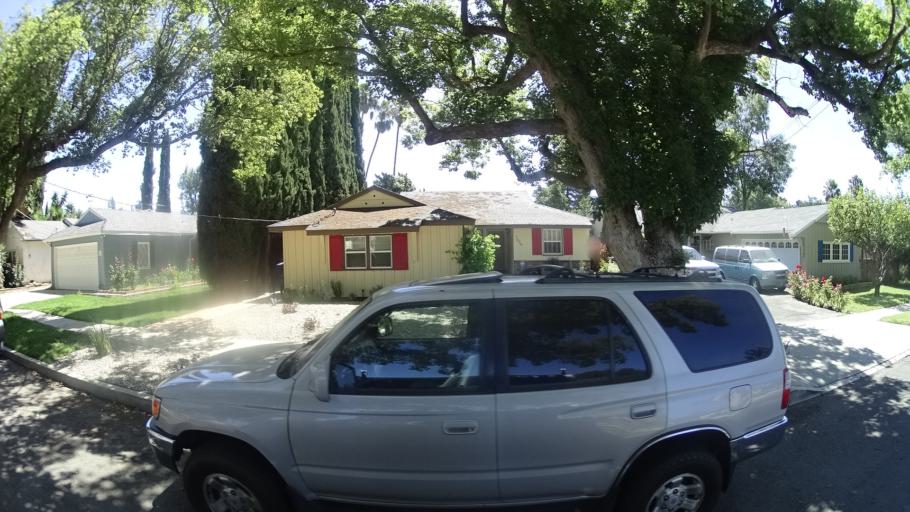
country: US
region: California
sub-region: Los Angeles County
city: Northridge
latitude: 34.1983
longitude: -118.5000
